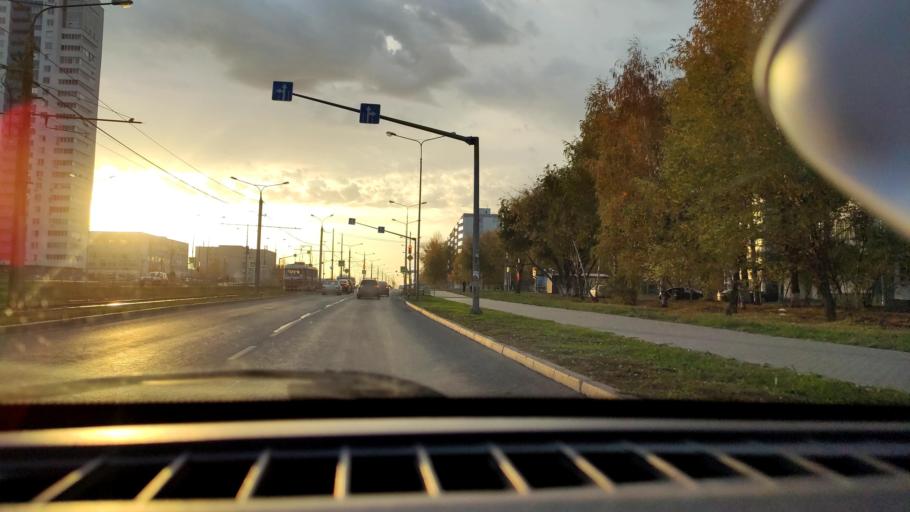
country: RU
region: Samara
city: Samara
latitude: 53.2664
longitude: 50.2290
